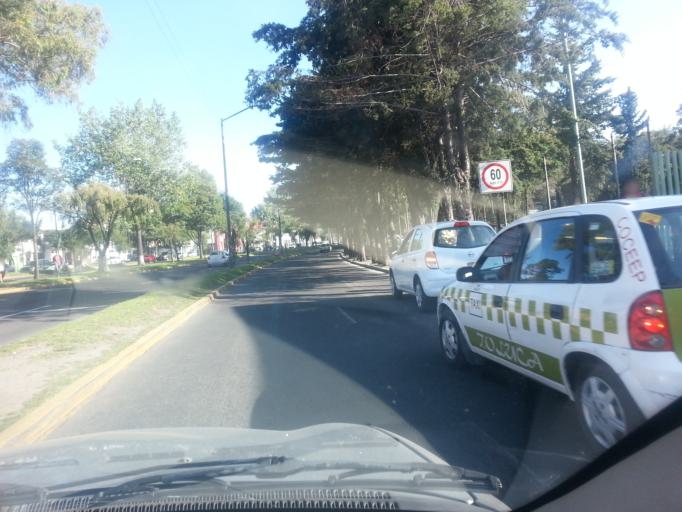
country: MX
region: Mexico
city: San Buenaventura
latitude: 19.2818
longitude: -99.6800
